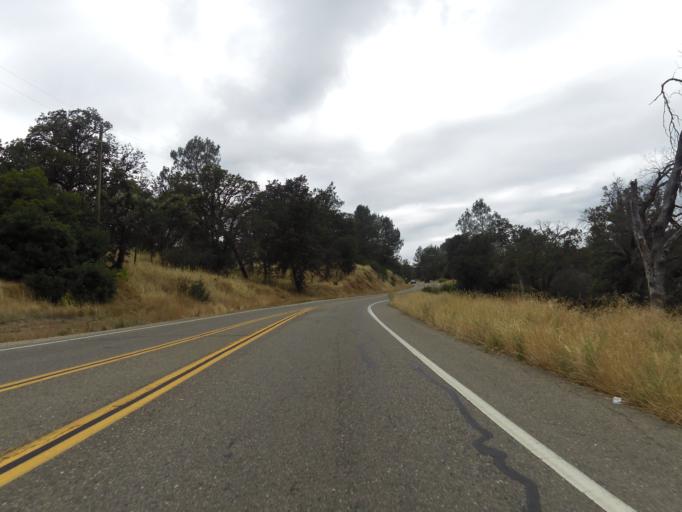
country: US
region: California
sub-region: Madera County
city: Coarsegold
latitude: 37.2625
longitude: -119.7092
